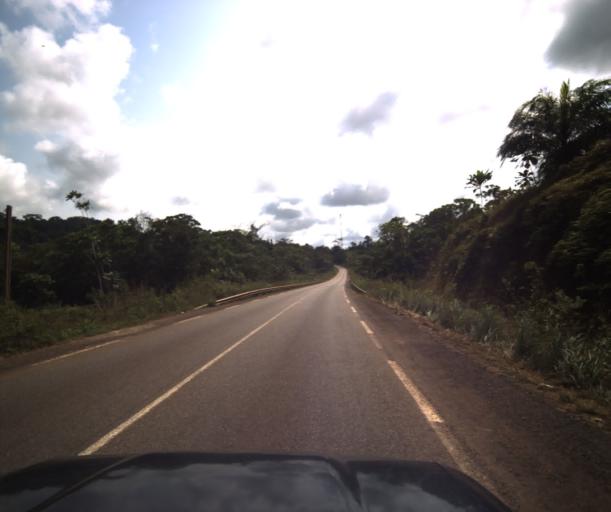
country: CM
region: Littoral
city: Edea
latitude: 3.7920
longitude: 10.2093
